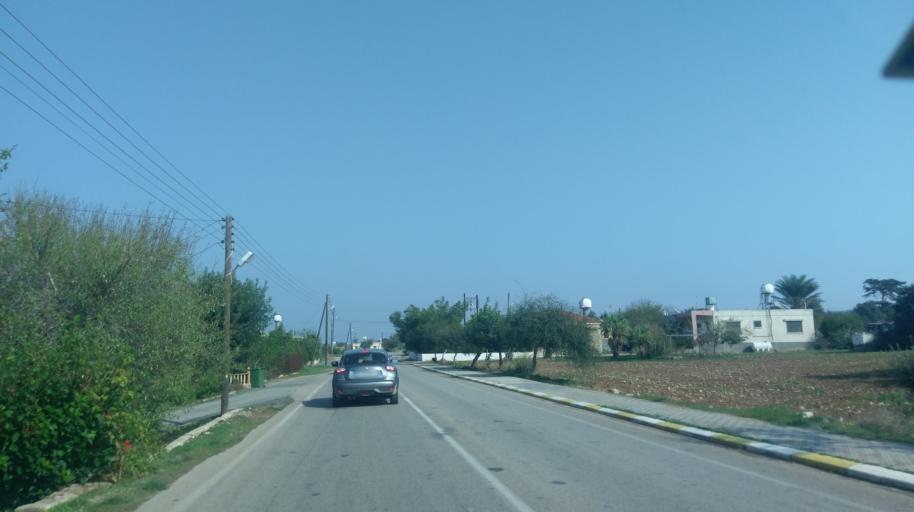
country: CY
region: Ammochostos
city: Leonarisso
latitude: 35.5264
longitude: 34.1801
